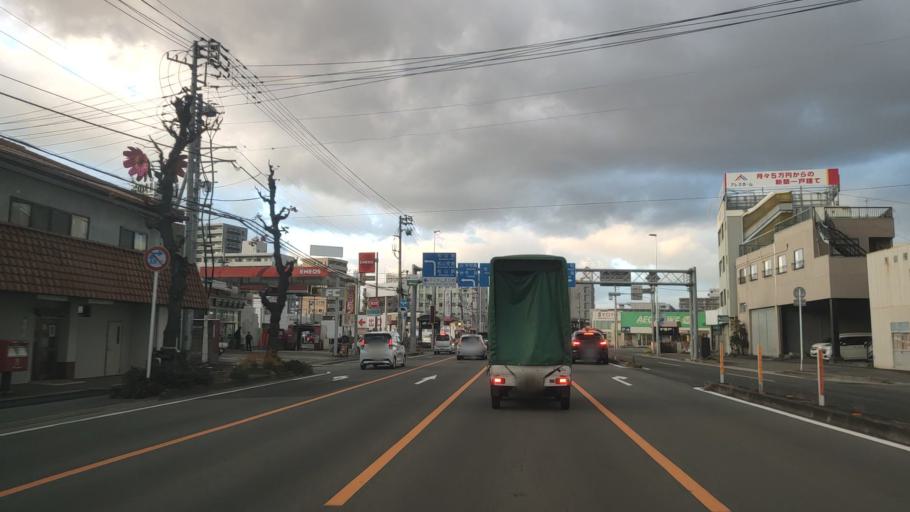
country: JP
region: Ehime
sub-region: Shikoku-chuo Shi
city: Matsuyama
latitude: 33.8214
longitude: 132.7760
